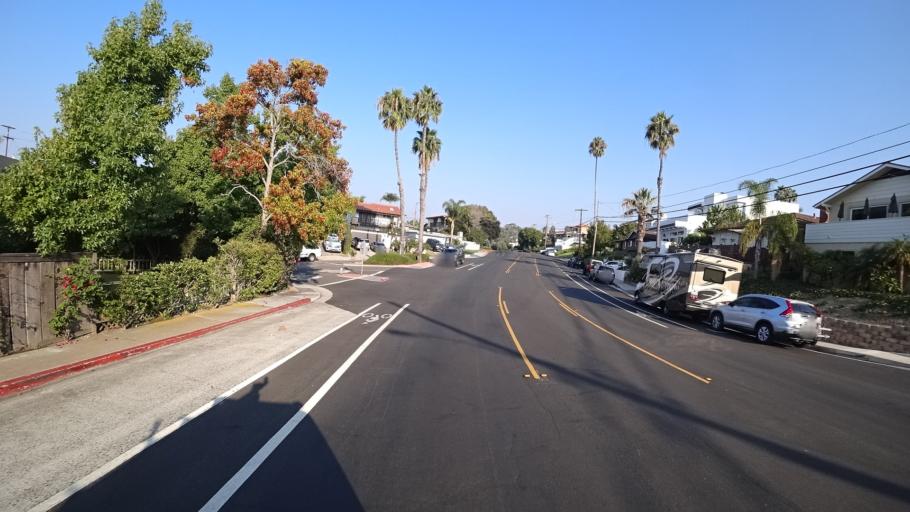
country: US
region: California
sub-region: Orange County
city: San Clemente
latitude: 33.4126
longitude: -117.6061
